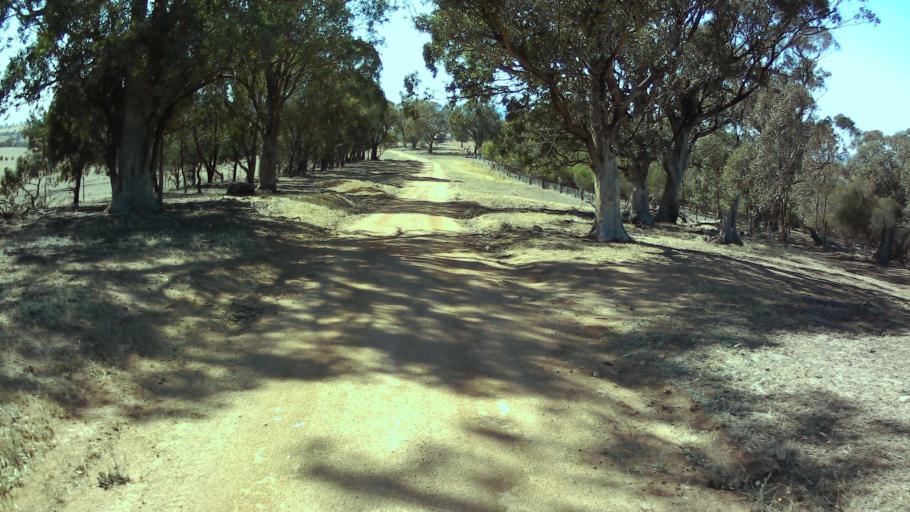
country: AU
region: New South Wales
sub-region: Cowra
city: Cowra
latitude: -33.9783
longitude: 148.4672
